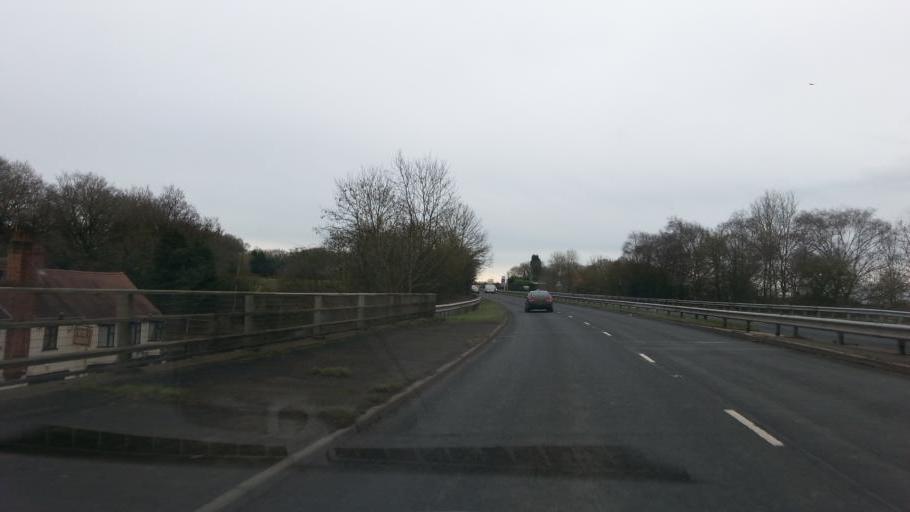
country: GB
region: England
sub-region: Solihull
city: Tidbury Green
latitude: 52.3611
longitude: -1.8894
